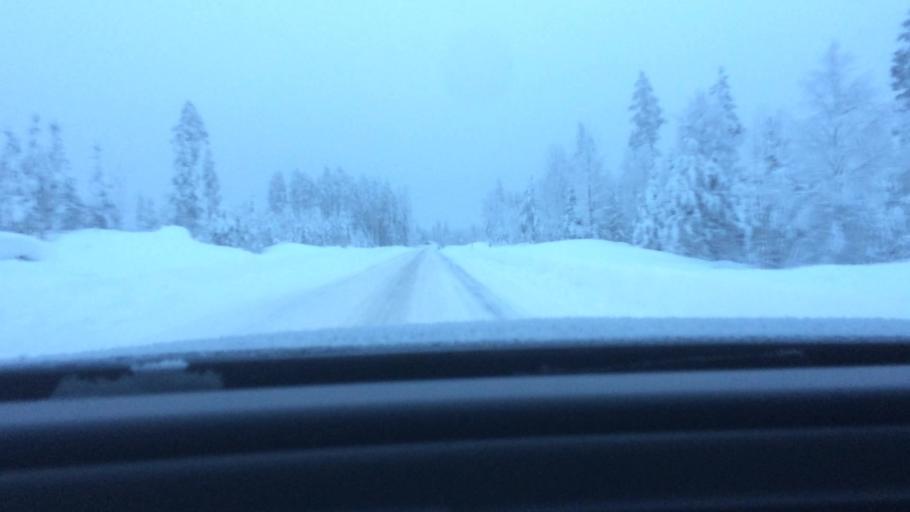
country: SE
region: Gaevleborg
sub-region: Ljusdals Kommun
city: Farila
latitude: 61.7755
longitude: 15.1729
